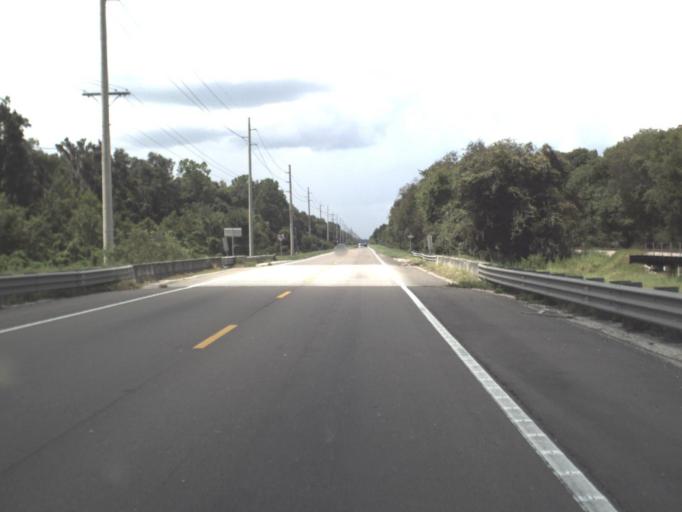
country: US
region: Florida
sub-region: Pasco County
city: Crystal Springs
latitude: 28.1401
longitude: -82.1500
